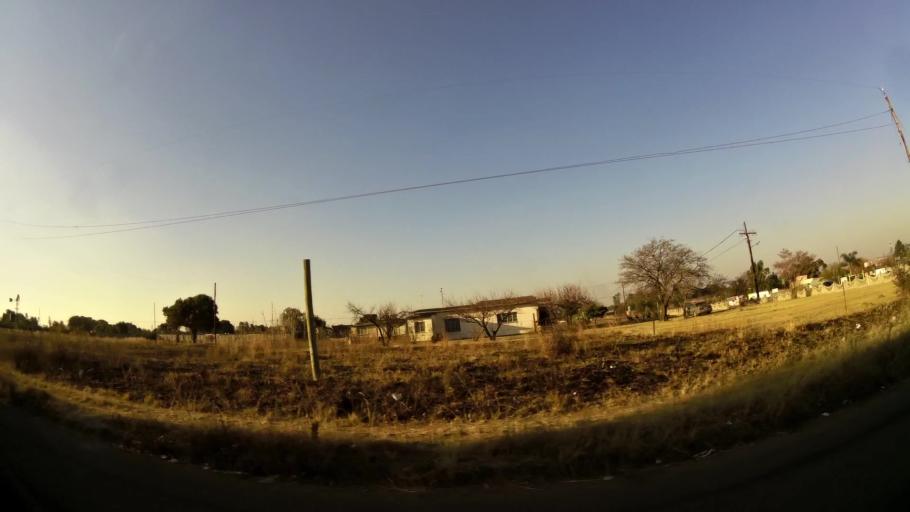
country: ZA
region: Gauteng
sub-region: West Rand District Municipality
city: Randfontein
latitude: -26.2174
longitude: 27.6461
